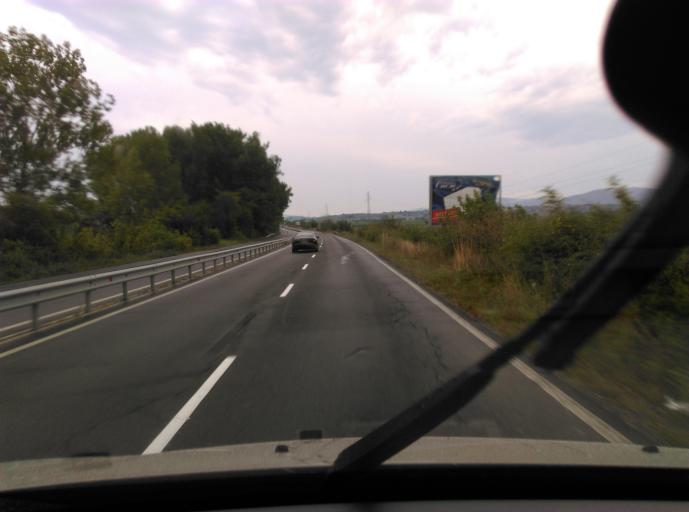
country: BG
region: Burgas
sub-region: Obshtina Sozopol
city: Chernomorets
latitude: 42.4148
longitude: 27.6456
